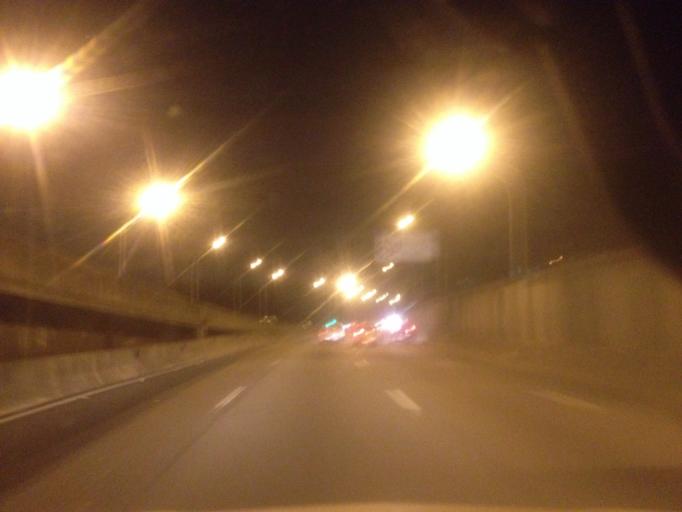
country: BR
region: Rio de Janeiro
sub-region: Rio De Janeiro
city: Rio de Janeiro
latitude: -22.8803
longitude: -43.2313
